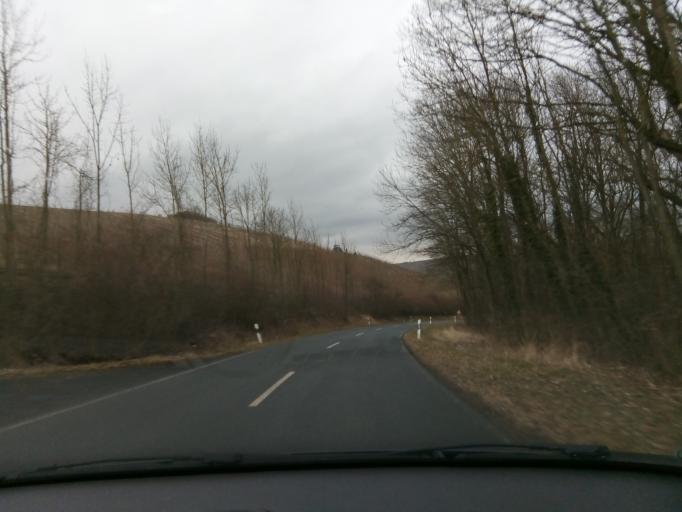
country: DE
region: Bavaria
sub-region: Regierungsbezirk Unterfranken
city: Sommerach
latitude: 49.8297
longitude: 10.1814
